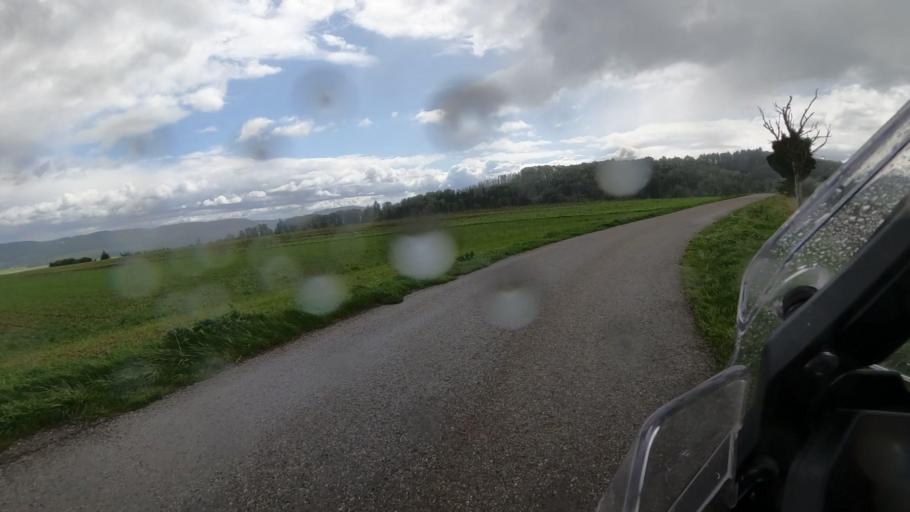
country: DE
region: Baden-Wuerttemberg
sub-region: Freiburg Region
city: Eggingen
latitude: 47.6677
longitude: 8.4068
